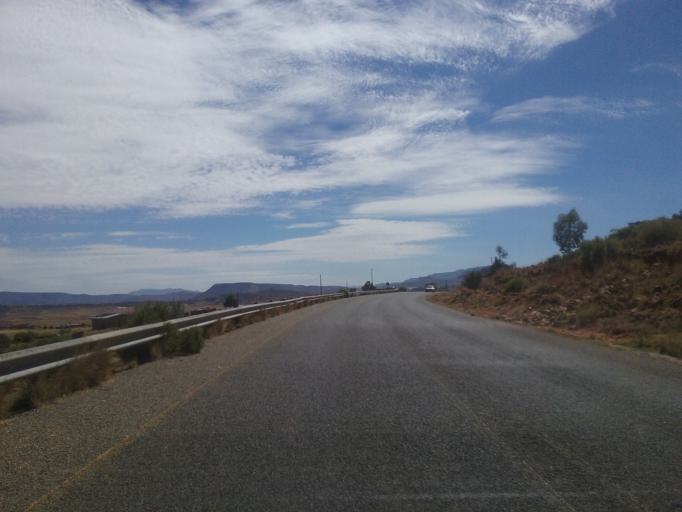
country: LS
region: Mohale's Hoek District
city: Mohale's Hoek
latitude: -30.1891
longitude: 27.4170
